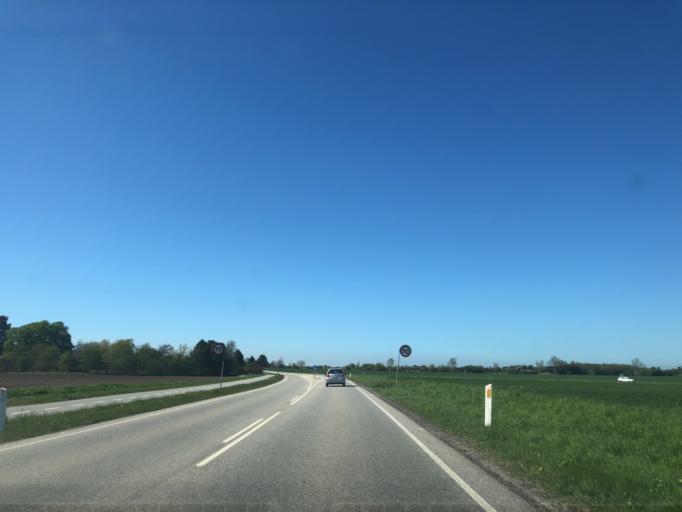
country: DK
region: Zealand
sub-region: Stevns Kommune
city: Store Heddinge
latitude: 55.3483
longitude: 12.3344
